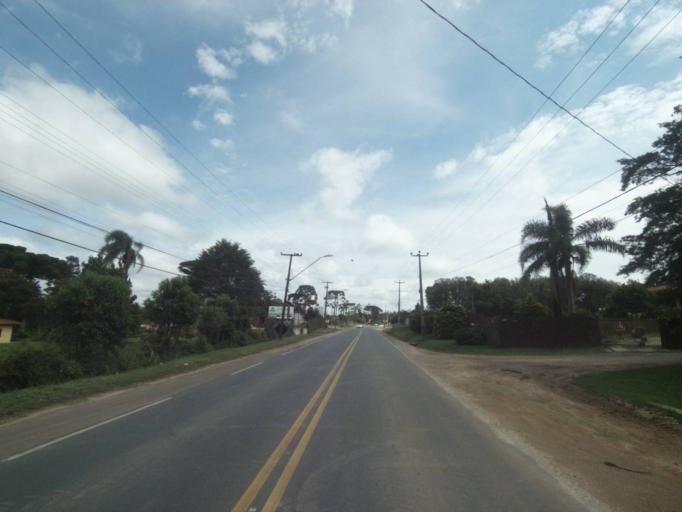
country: BR
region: Parana
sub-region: Quatro Barras
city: Quatro Barras
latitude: -25.3377
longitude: -49.0801
